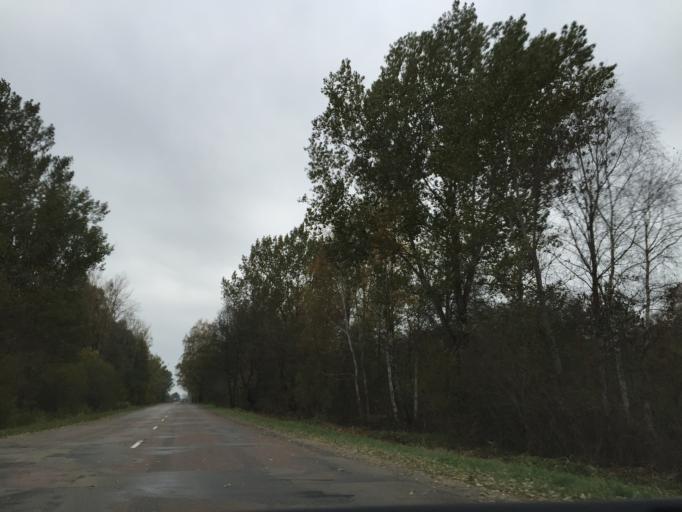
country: LV
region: Marupe
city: Marupe
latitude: 56.8524
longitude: 24.0535
